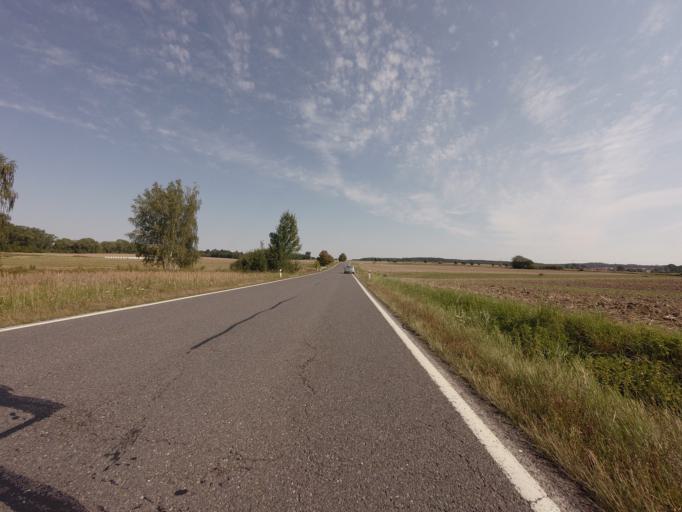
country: CZ
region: Jihocesky
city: Bernartice
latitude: 49.3934
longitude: 14.3607
